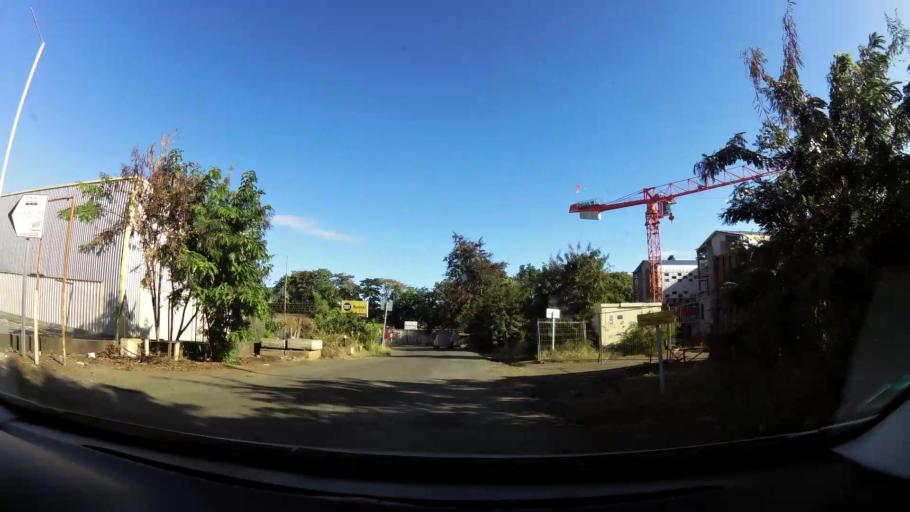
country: YT
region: Mamoudzou
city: Mamoudzou
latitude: -12.7650
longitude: 45.2270
